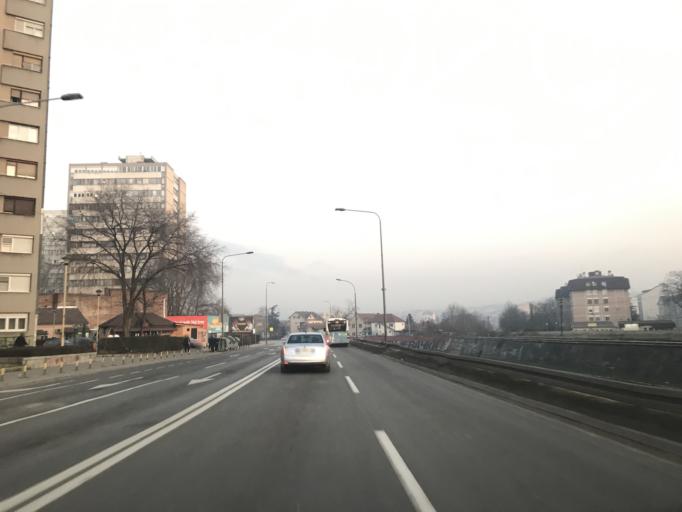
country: RS
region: Central Serbia
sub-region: Sumadijski Okrug
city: Kragujevac
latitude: 44.0090
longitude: 20.9146
